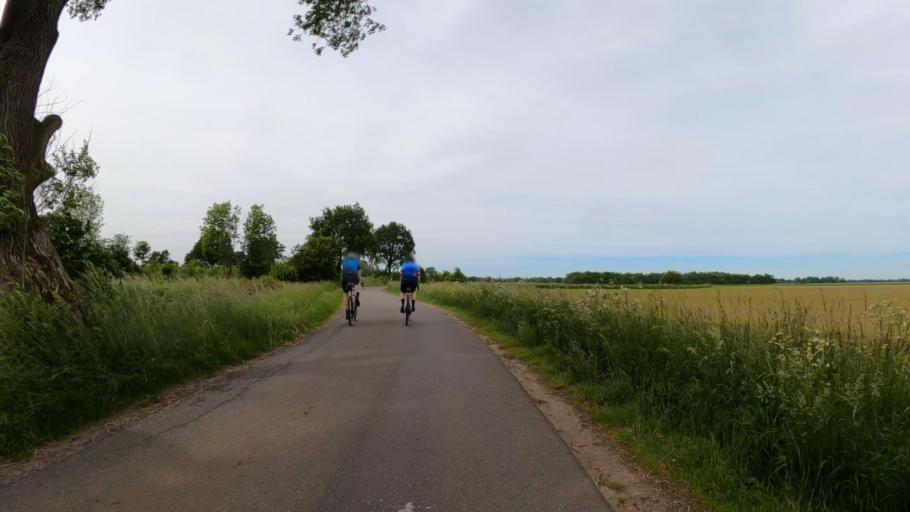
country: DE
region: Schleswig-Holstein
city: Sievershutten
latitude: 53.8715
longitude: 10.0859
